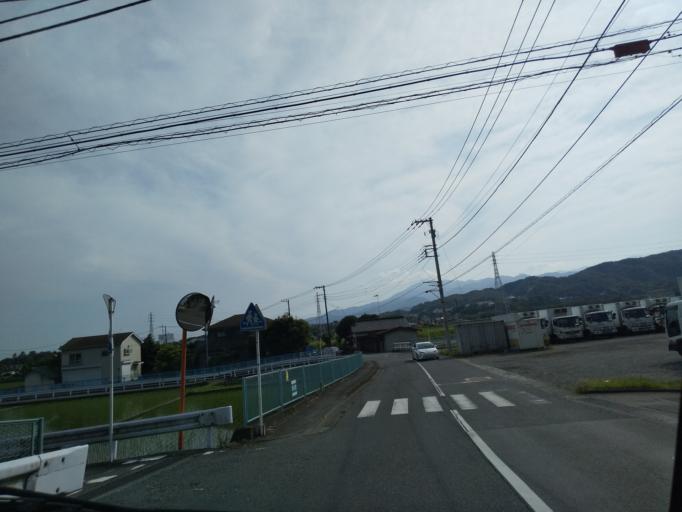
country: JP
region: Kanagawa
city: Zama
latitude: 35.5013
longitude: 139.3516
